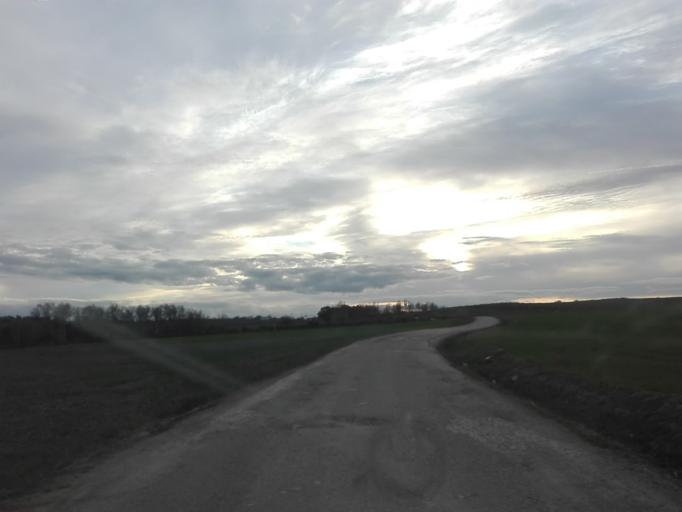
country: ES
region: Extremadura
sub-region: Provincia de Badajoz
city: Usagre
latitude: 38.3580
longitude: -6.1723
